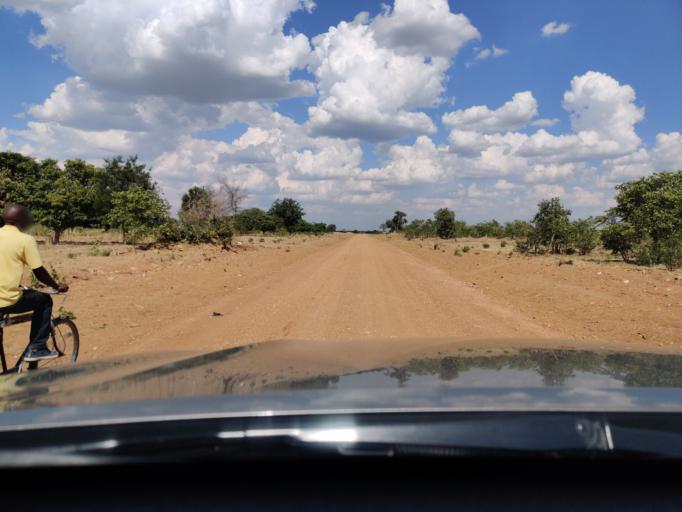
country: ZM
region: Central
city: Chibombo
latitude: -14.7593
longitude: 27.8736
